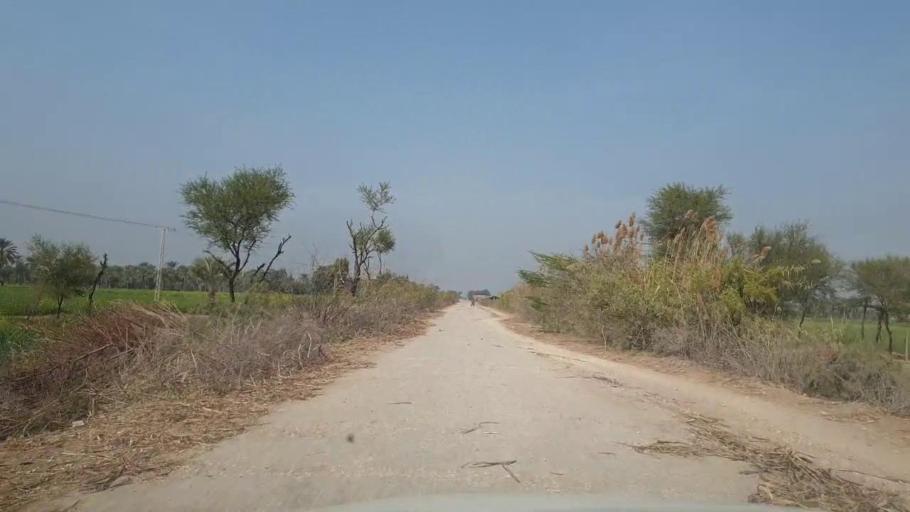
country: PK
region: Sindh
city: Mirpur Khas
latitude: 25.6818
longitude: 69.1551
